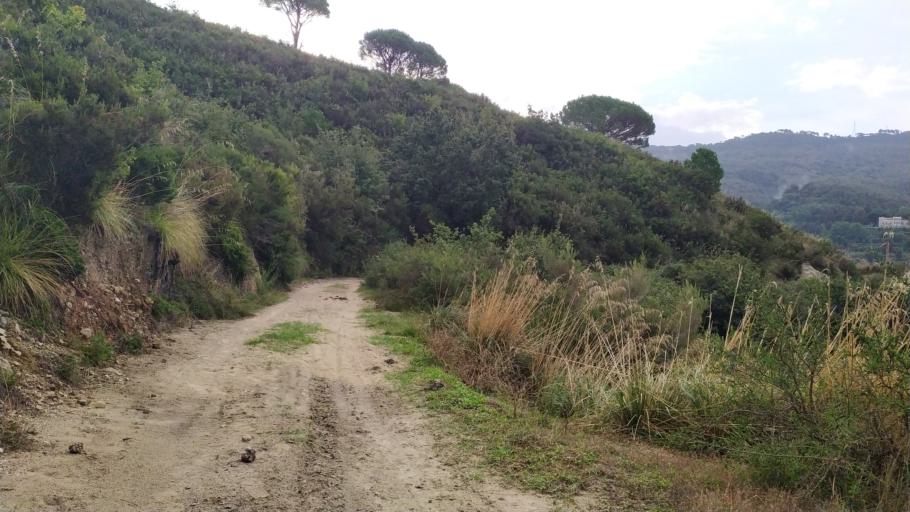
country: IT
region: Sicily
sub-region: Messina
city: Saponara
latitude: 38.2110
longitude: 15.4792
